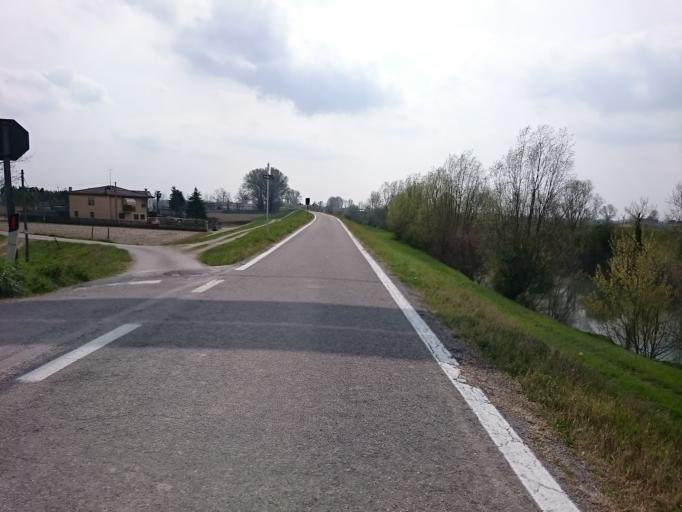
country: IT
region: Veneto
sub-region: Provincia di Padova
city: Bovolenta
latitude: 45.2916
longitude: 11.9283
